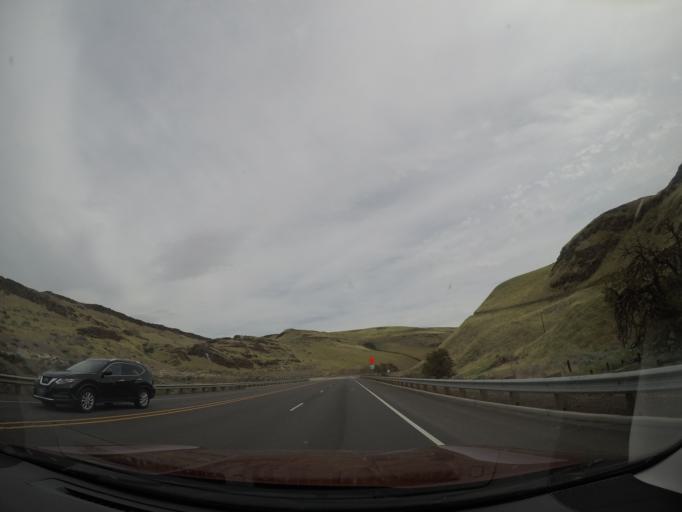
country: US
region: Washington
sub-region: Klickitat County
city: Goldendale
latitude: 45.6683
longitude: -120.8285
